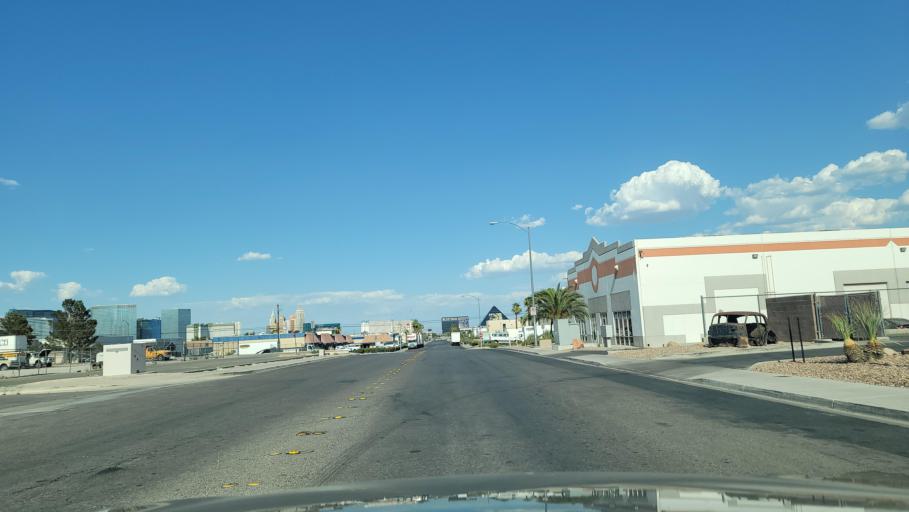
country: US
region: Nevada
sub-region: Clark County
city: Spring Valley
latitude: 36.0972
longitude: -115.2032
